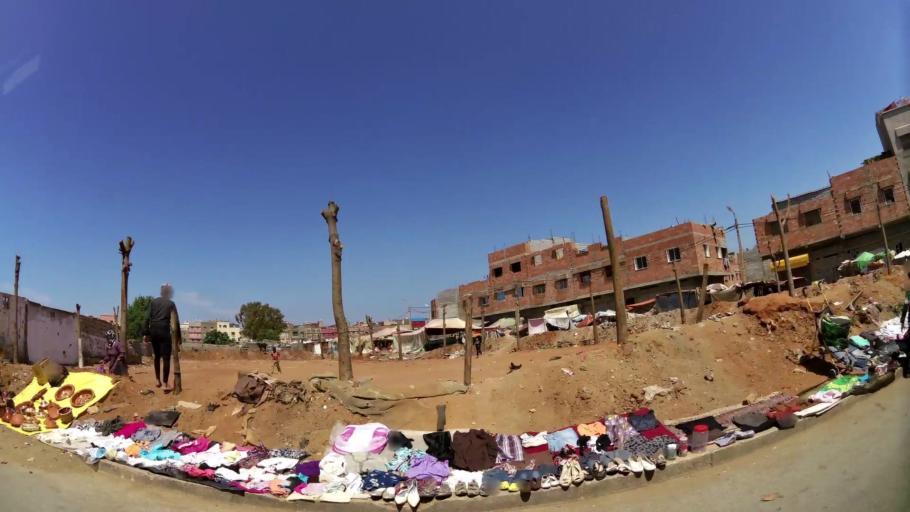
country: MA
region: Rabat-Sale-Zemmour-Zaer
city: Sale
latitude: 34.0604
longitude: -6.7780
